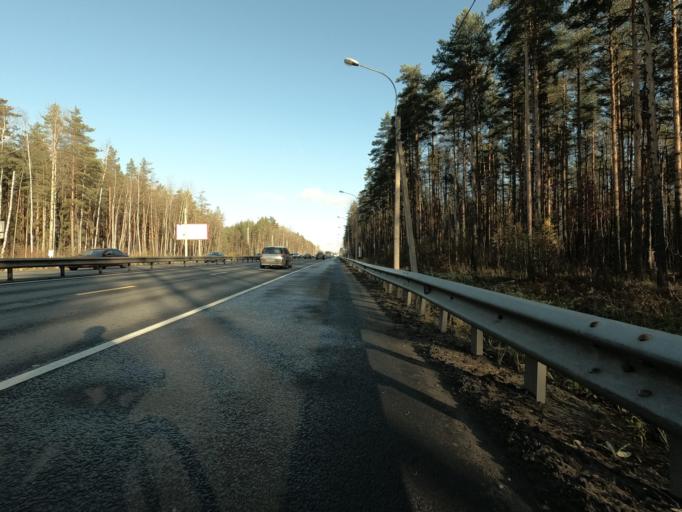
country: RU
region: St.-Petersburg
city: Krasnogvargeisky
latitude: 60.0021
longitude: 30.5579
